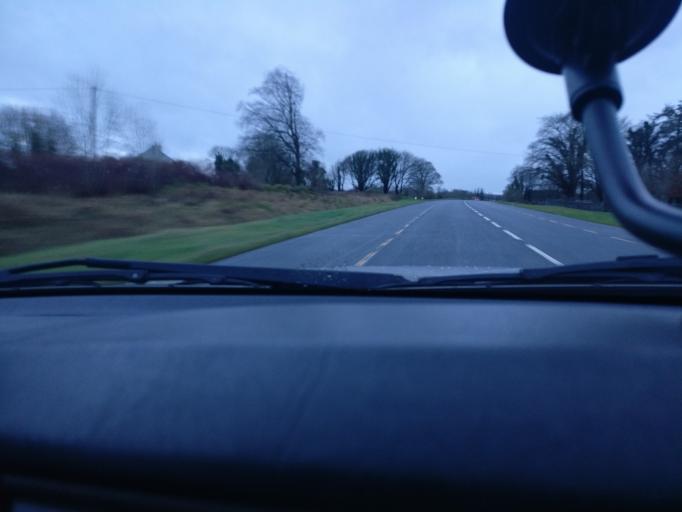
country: IE
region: Connaught
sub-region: County Galway
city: Ballinasloe
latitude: 53.2948
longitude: -8.3279
